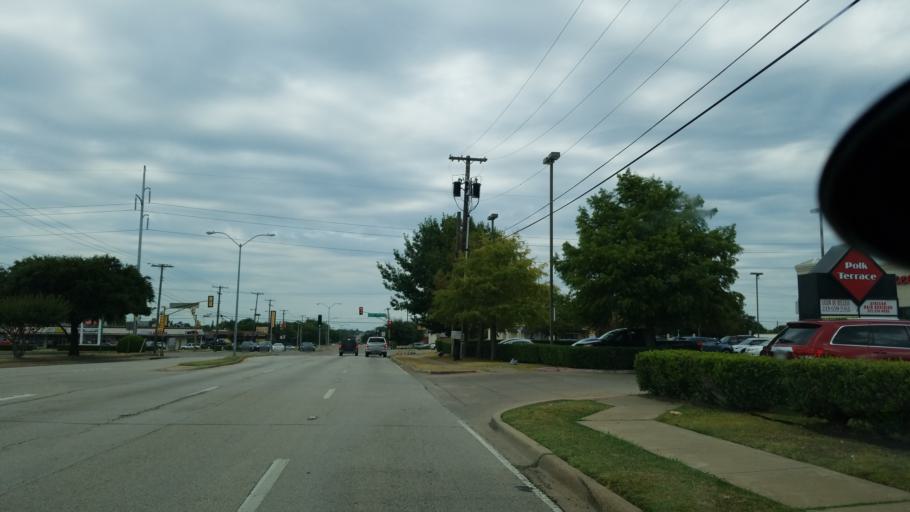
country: US
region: Texas
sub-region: Dallas County
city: Duncanville
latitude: 32.6612
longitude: -96.8399
